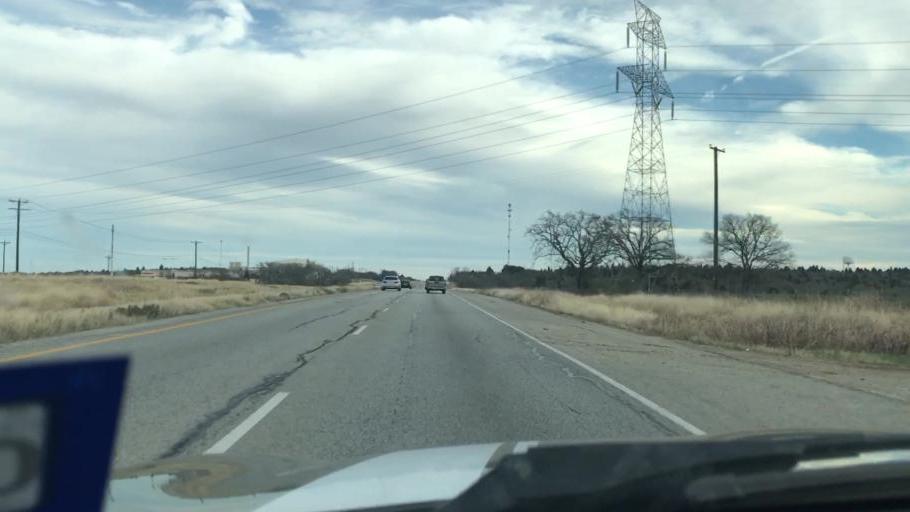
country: US
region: Texas
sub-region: Bastrop County
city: Elgin
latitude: 30.3307
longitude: -97.3472
